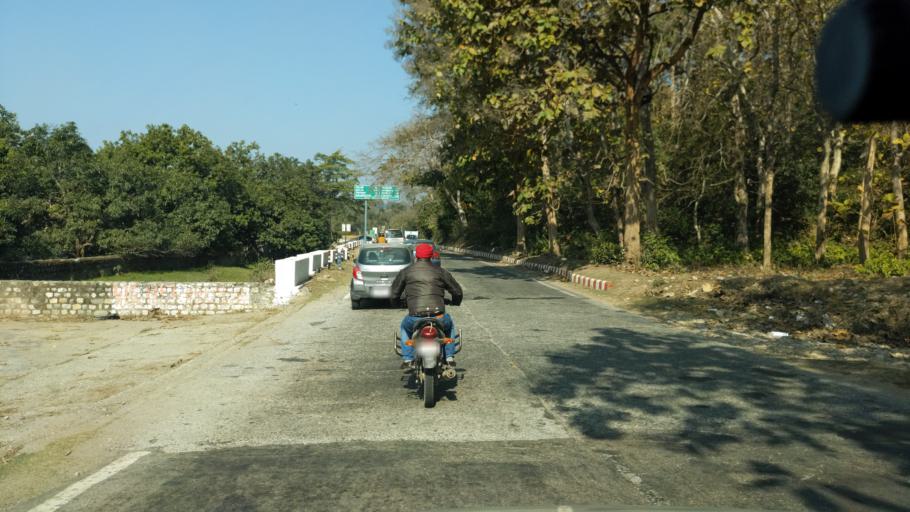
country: IN
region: Uttarakhand
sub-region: Naini Tal
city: Ramnagar
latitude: 29.3896
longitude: 79.1393
